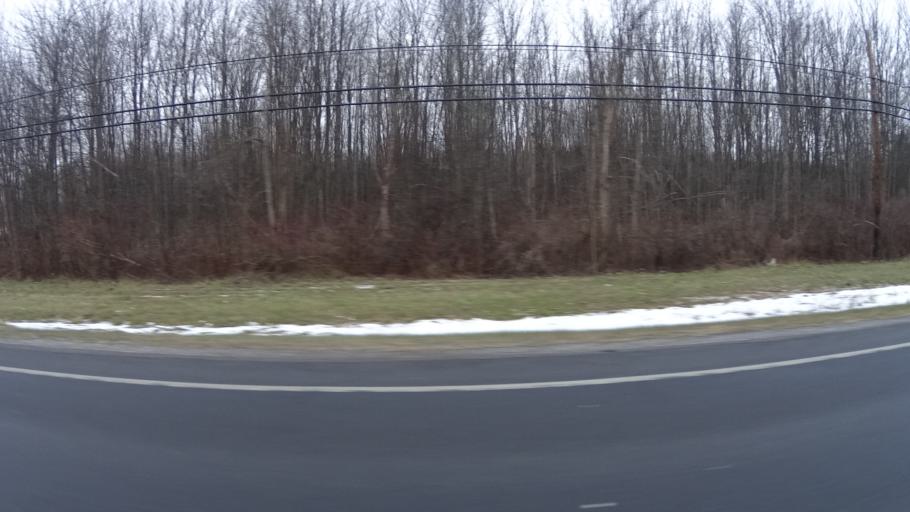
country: US
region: Ohio
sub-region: Lorain County
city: Eaton Estates
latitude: 41.3141
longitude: -82.0126
